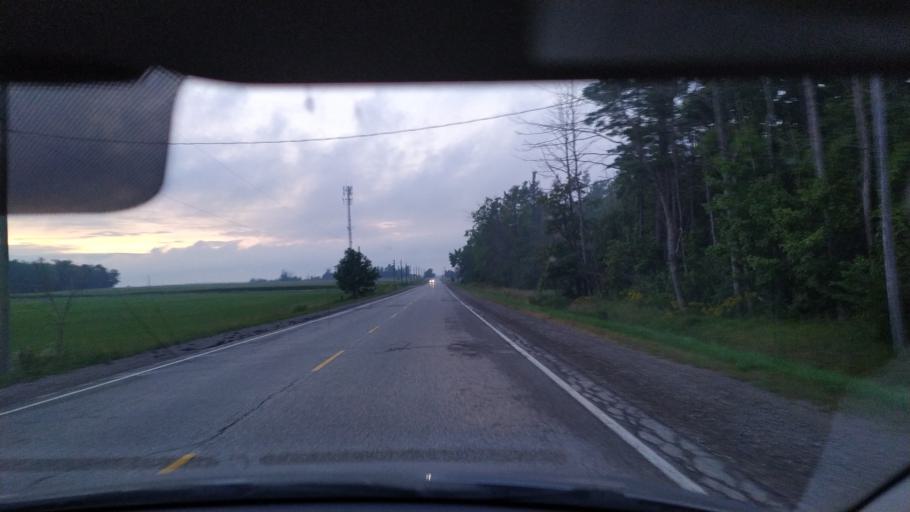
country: CA
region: Ontario
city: Kitchener
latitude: 43.3594
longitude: -80.7057
